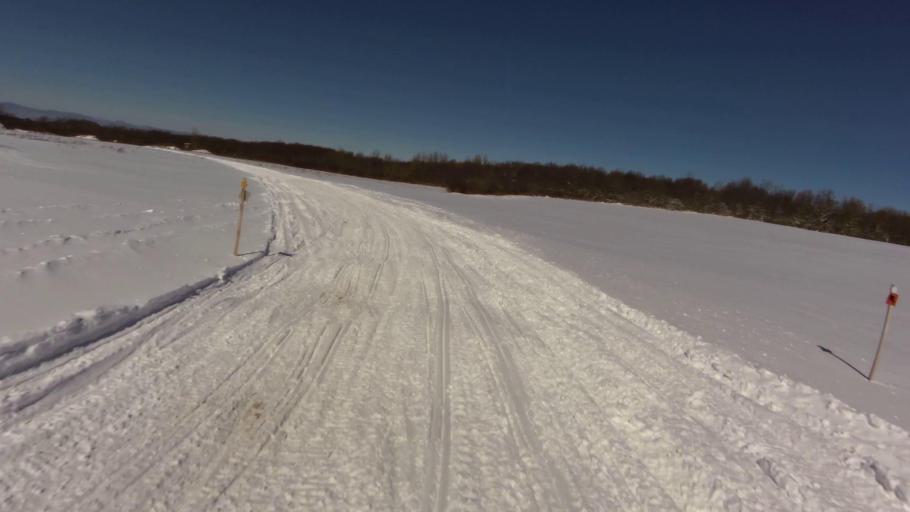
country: US
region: New York
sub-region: Chautauqua County
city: Mayville
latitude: 42.2655
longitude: -79.4508
